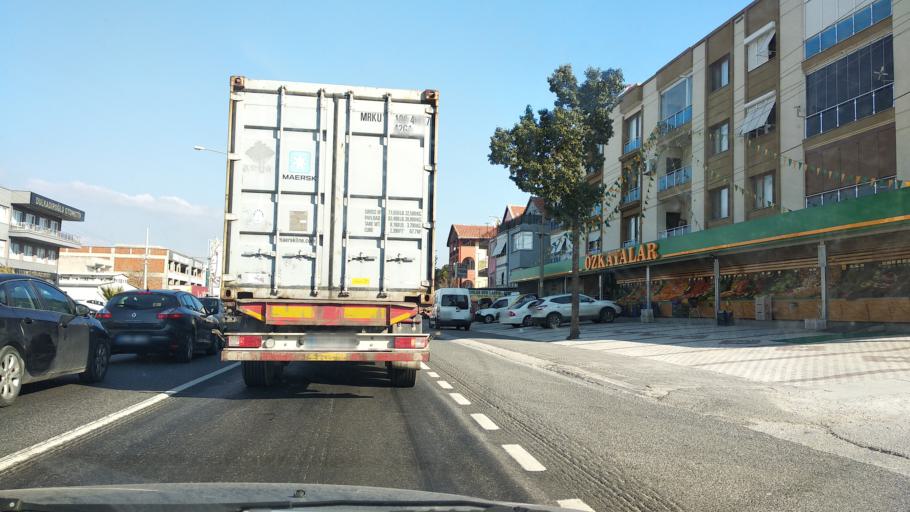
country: TR
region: Izmir
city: Menemen
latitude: 38.5755
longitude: 27.0621
